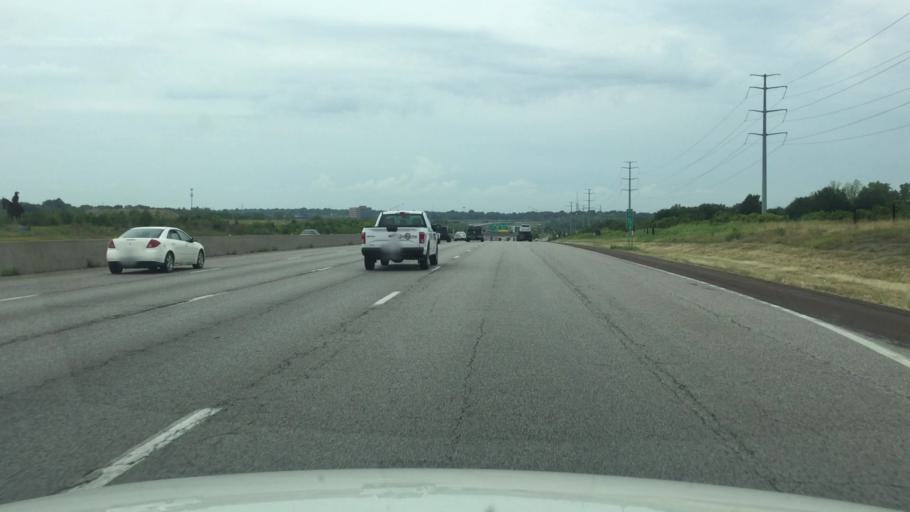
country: US
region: Missouri
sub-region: Jackson County
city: Grandview
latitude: 38.9601
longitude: -94.5251
